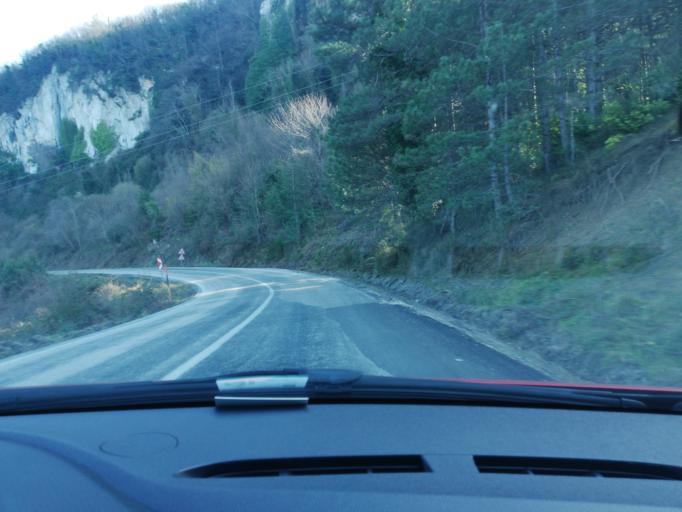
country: TR
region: Bartin
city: Kurucasile
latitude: 41.8452
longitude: 32.7645
